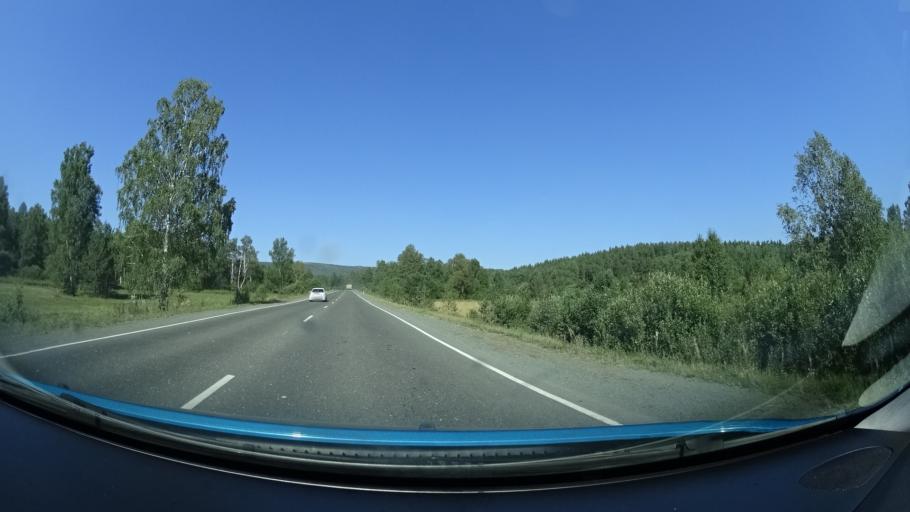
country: RU
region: Bashkortostan
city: Abzakovo
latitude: 53.8587
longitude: 58.5606
